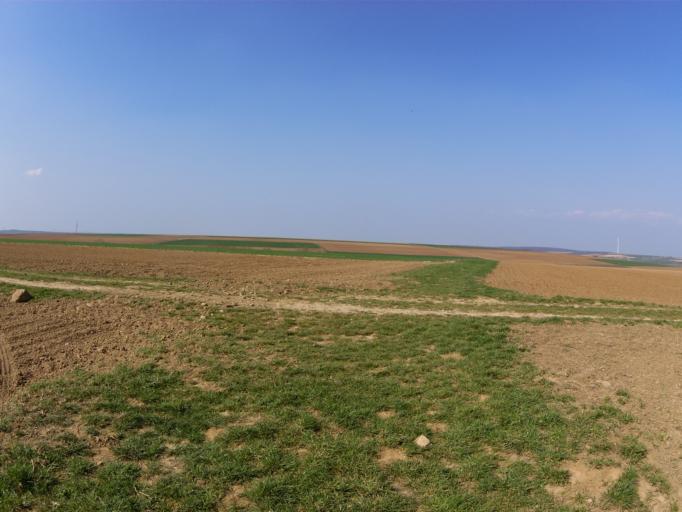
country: DE
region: Bavaria
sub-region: Regierungsbezirk Unterfranken
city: Mainstockheim
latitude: 49.7905
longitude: 10.1412
